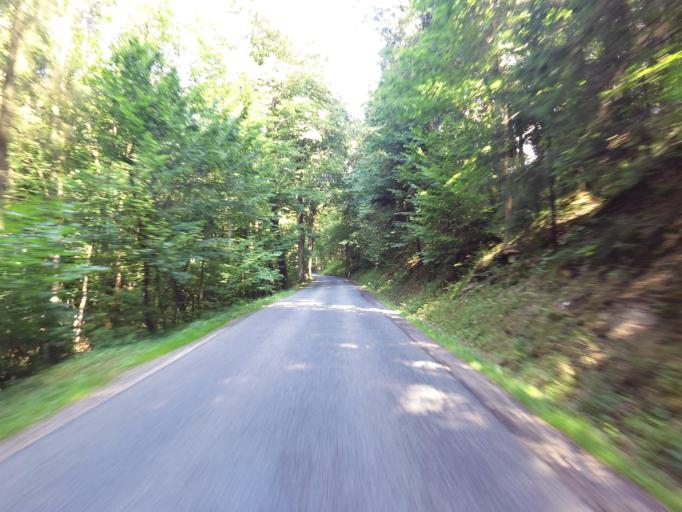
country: CZ
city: Cesky Dub
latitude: 50.6128
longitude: 14.9957
